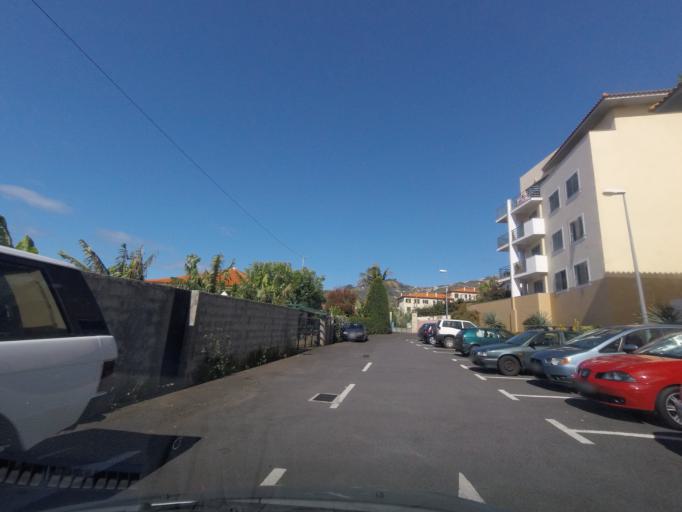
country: PT
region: Madeira
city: Camara de Lobos
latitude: 32.6590
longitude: -16.9730
